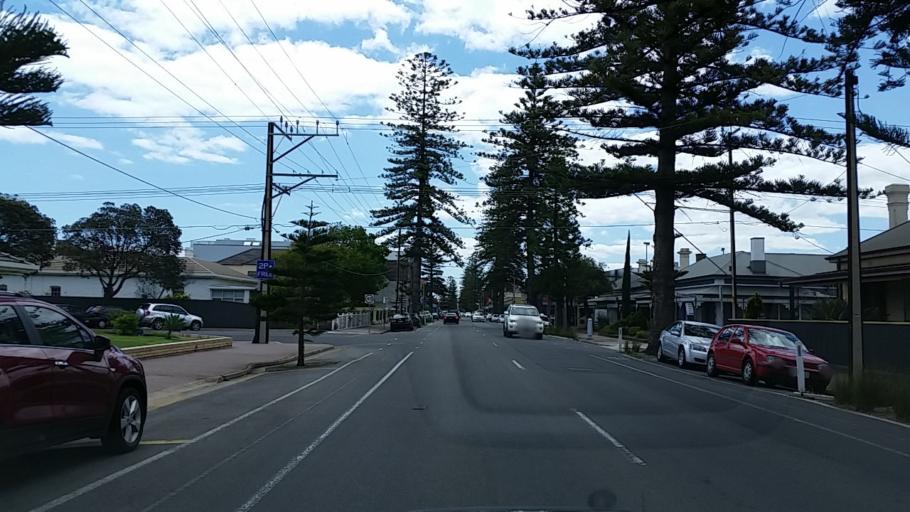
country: AU
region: South Australia
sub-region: Adelaide
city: Glenelg
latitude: -34.9820
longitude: 138.5179
